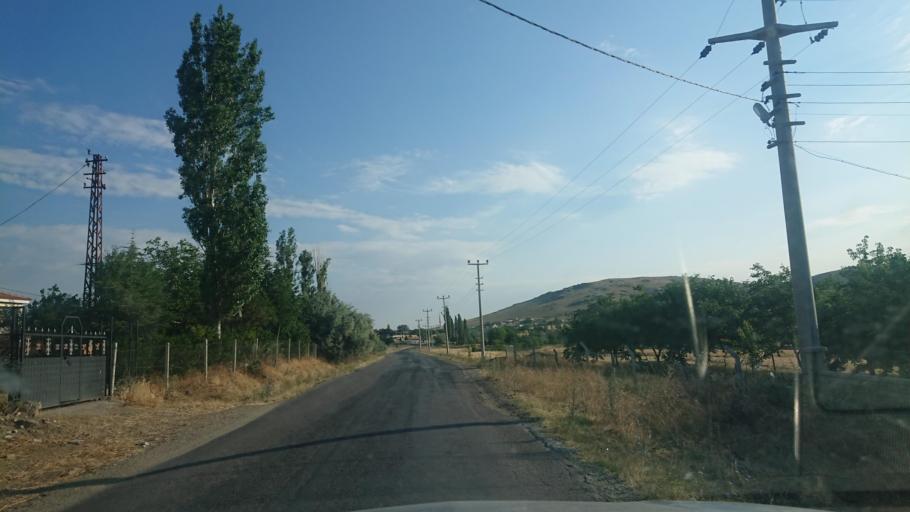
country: TR
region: Aksaray
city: Ortakoy
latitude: 38.7633
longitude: 34.0614
